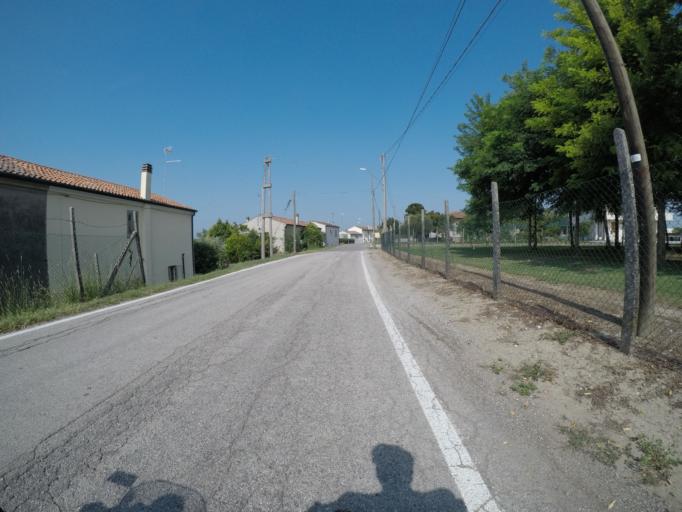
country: IT
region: Veneto
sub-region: Provincia di Rovigo
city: Lendinara
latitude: 45.0728
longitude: 11.6049
